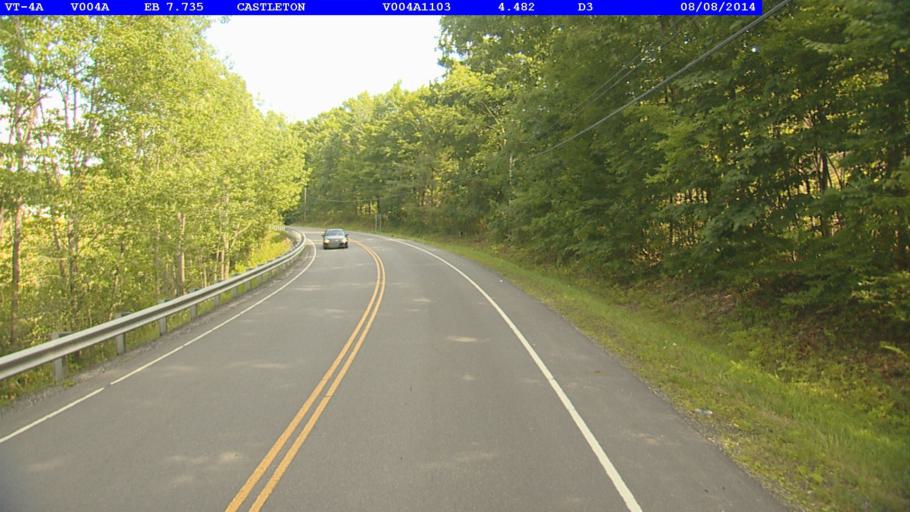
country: US
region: Vermont
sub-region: Rutland County
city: Castleton
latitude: 43.6117
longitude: -73.1581
